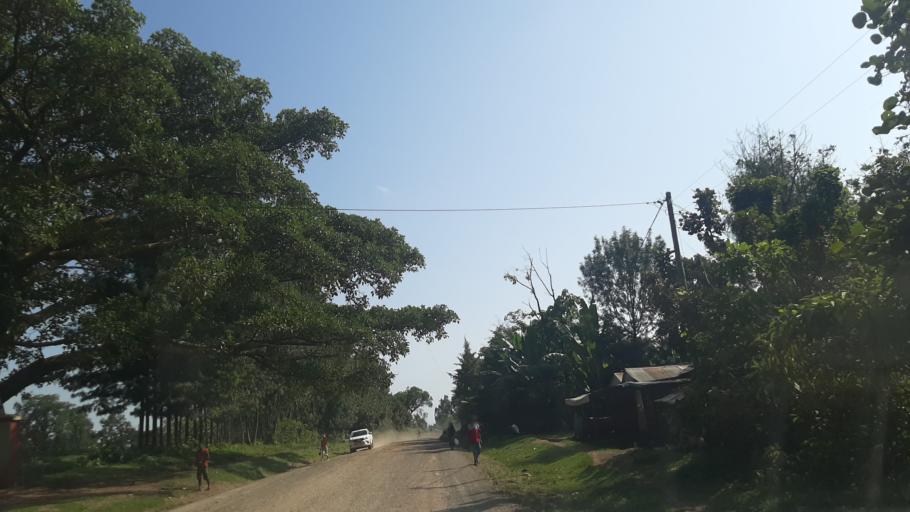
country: ET
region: Oromiya
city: Jima
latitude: 7.7731
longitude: 36.8005
